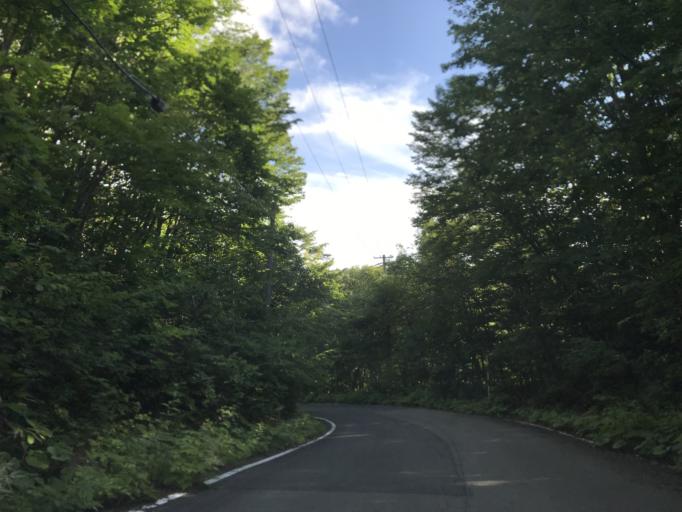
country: JP
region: Iwate
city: Ichinoseki
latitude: 38.9173
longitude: 140.8283
